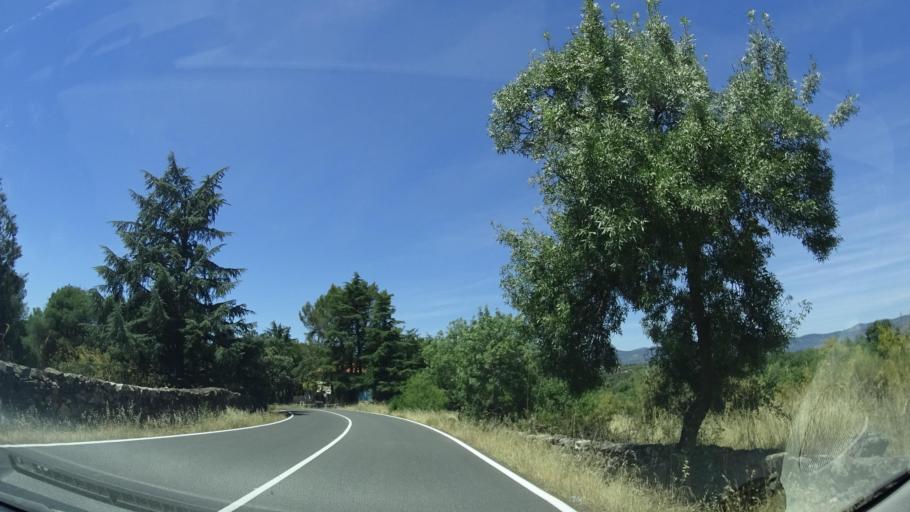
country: ES
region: Madrid
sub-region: Provincia de Madrid
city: Galapagar
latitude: 40.6063
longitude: -3.9806
